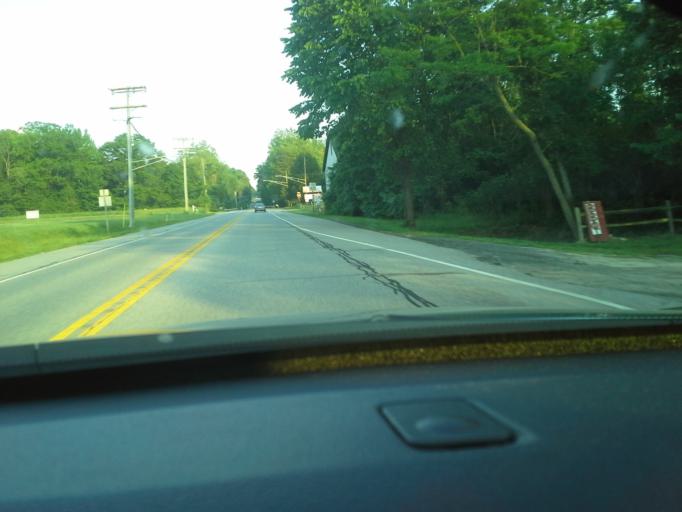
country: US
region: Maryland
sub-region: Calvert County
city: Owings
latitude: 38.7171
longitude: -76.6009
